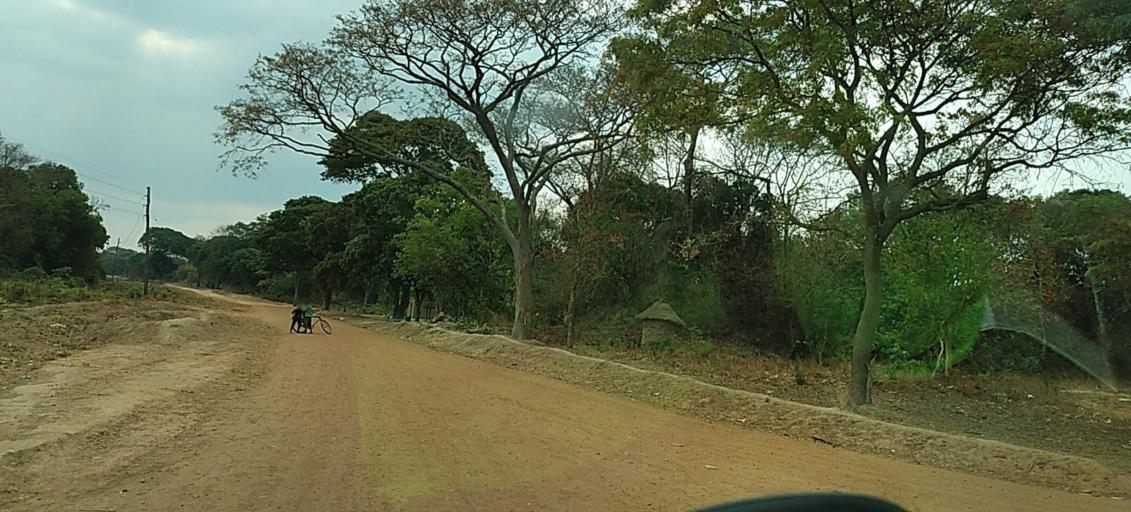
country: ZM
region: North-Western
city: Solwezi
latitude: -12.7855
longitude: 26.5145
